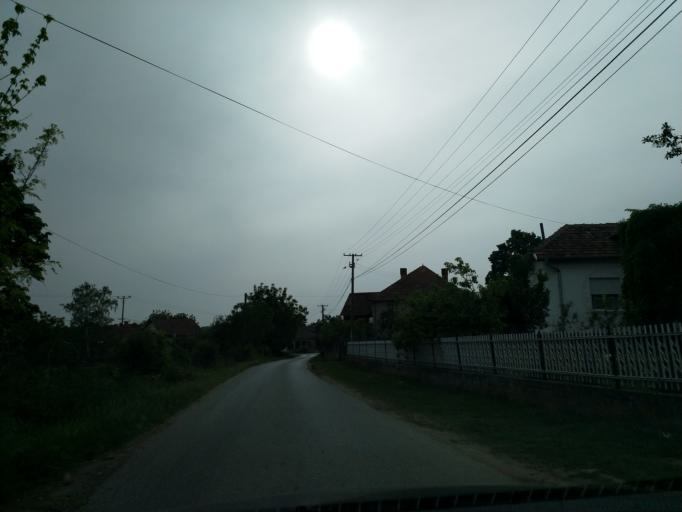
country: RS
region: Central Serbia
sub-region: Pomoravski Okrug
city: Jagodina
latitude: 43.9669
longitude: 21.2312
